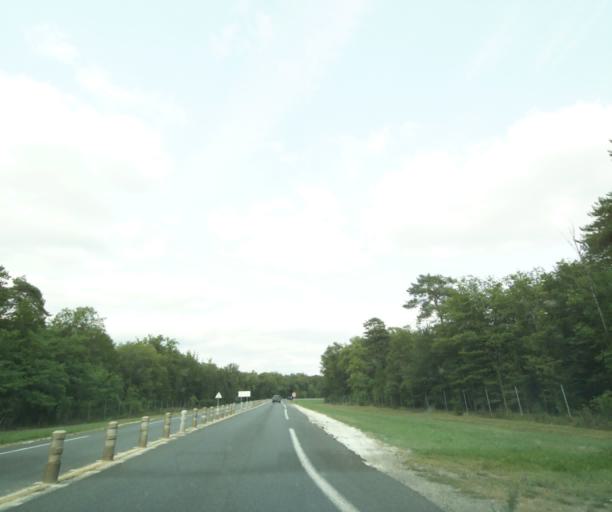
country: FR
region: Centre
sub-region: Departement d'Indre-et-Loire
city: Esvres
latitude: 47.3067
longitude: 0.7901
